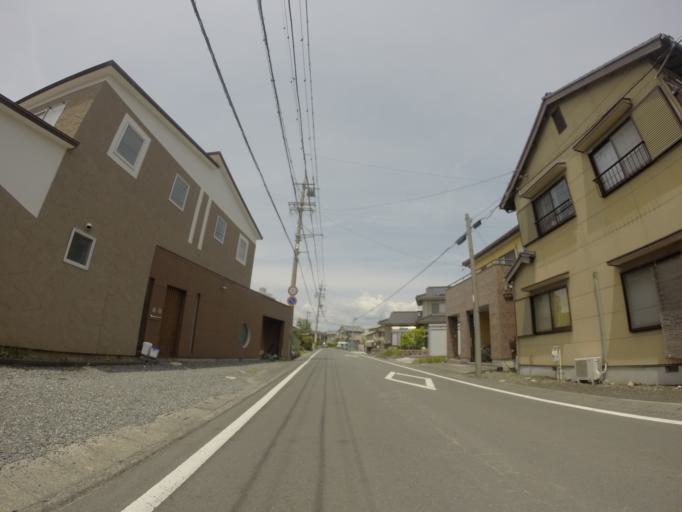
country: JP
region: Shizuoka
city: Fujieda
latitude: 34.8714
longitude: 138.2762
